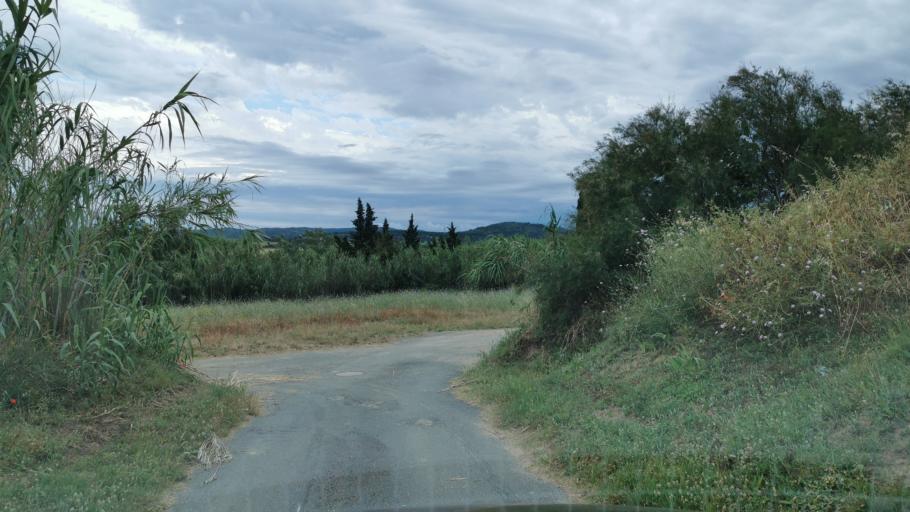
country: FR
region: Languedoc-Roussillon
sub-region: Departement de l'Aude
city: Marcorignan
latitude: 43.2228
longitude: 2.9279
